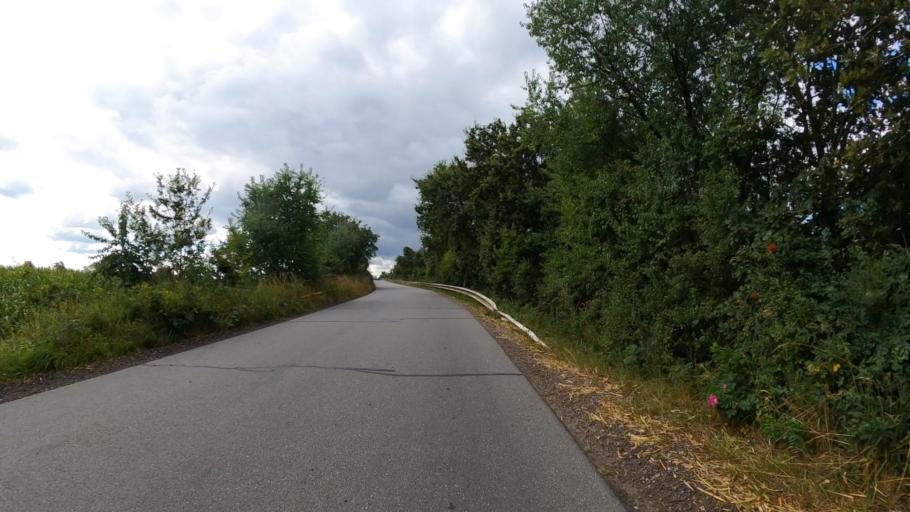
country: DE
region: Schleswig-Holstein
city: Padenstedt
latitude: 54.0399
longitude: 9.9163
